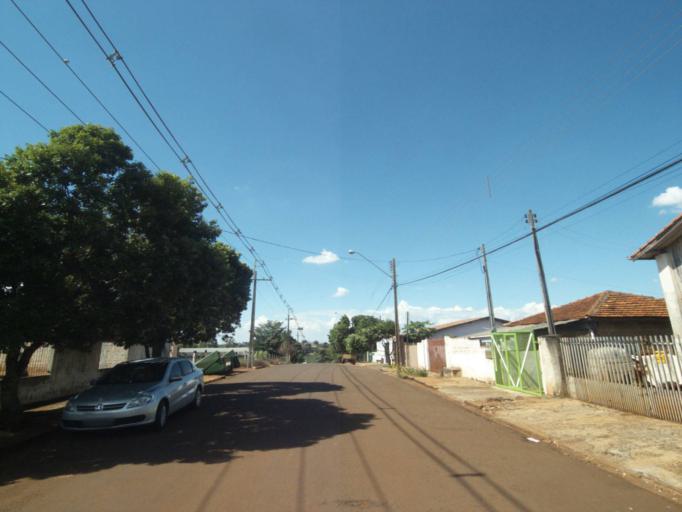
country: BR
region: Parana
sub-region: Sertanopolis
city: Sertanopolis
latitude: -23.0437
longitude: -50.8221
